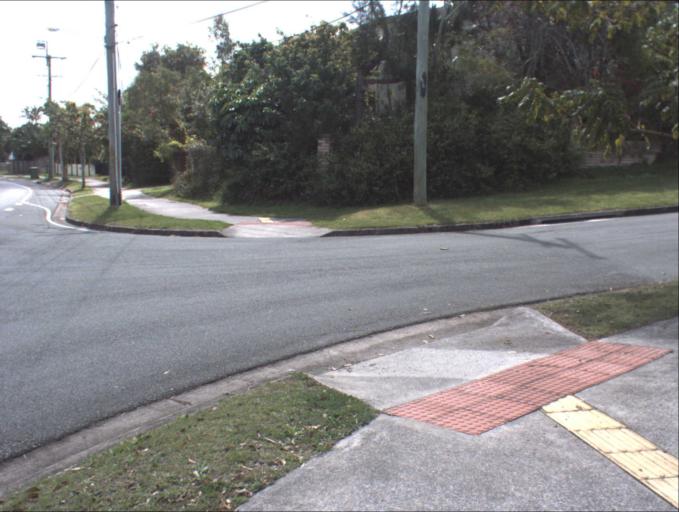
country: AU
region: Queensland
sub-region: Logan
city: Waterford West
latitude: -27.6843
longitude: 153.1483
